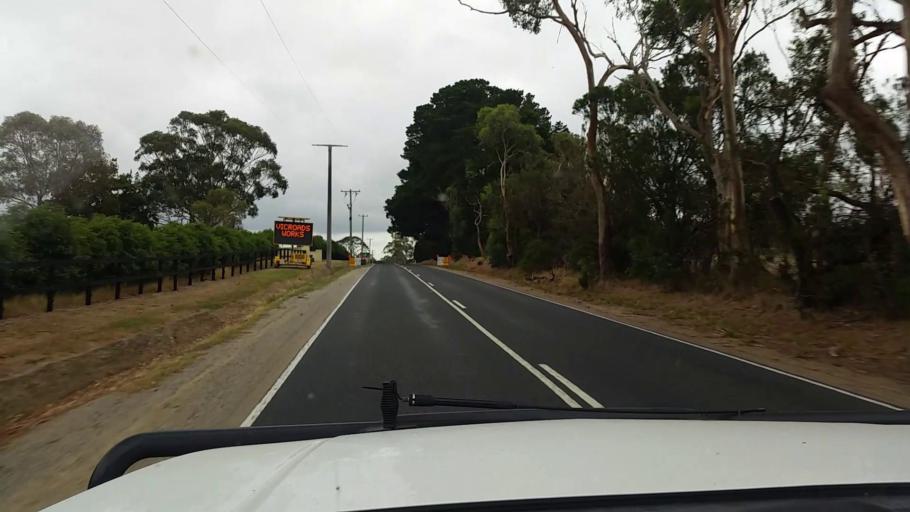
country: AU
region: Victoria
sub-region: Mornington Peninsula
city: Tyabb
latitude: -38.2627
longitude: 145.1456
